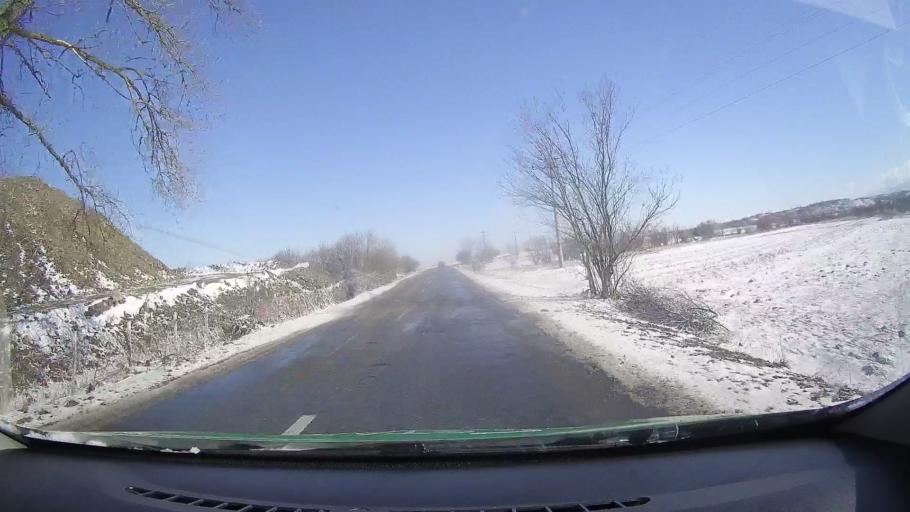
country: RO
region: Sibiu
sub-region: Comuna Racovita
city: Racovita
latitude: 45.6736
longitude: 24.3246
